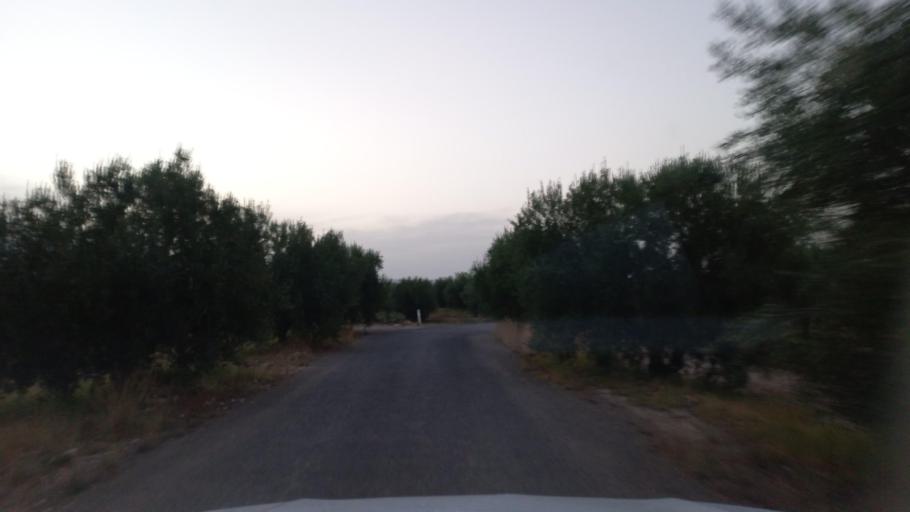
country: TN
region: Al Qasrayn
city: Kasserine
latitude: 35.2717
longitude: 9.0306
